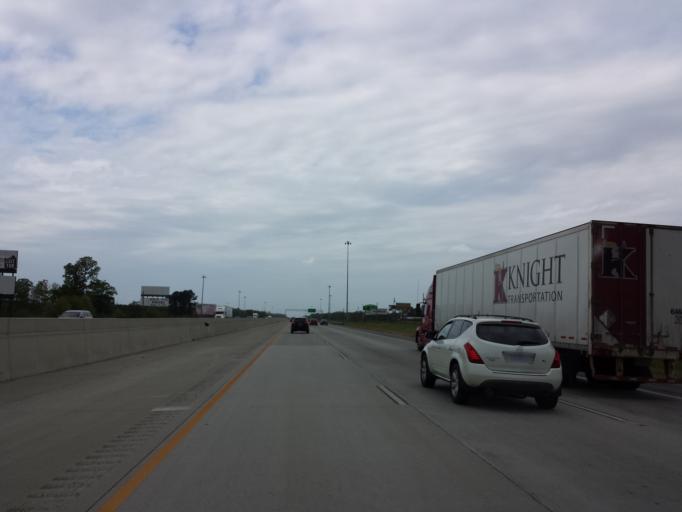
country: US
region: Georgia
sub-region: Crisp County
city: Cordele
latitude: 31.9953
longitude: -83.7570
